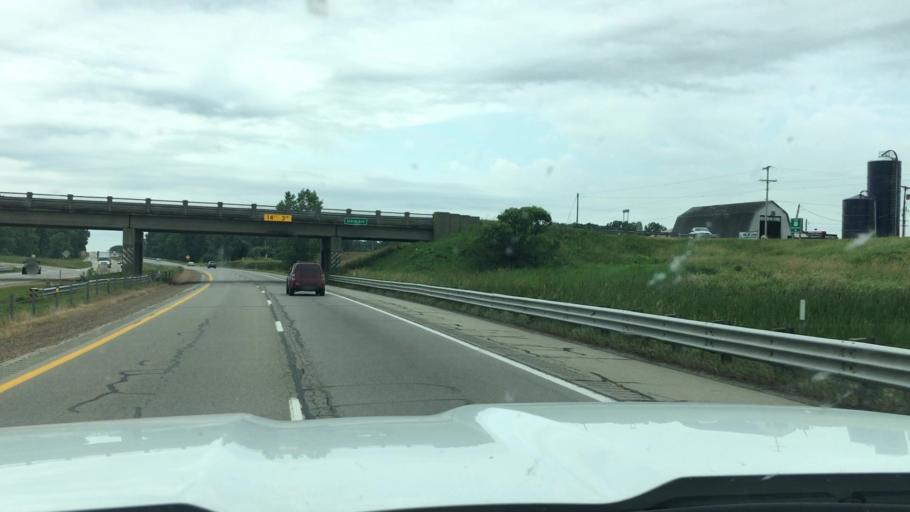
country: US
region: Michigan
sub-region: Allegan County
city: Wayland
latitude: 42.5950
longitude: -85.6627
